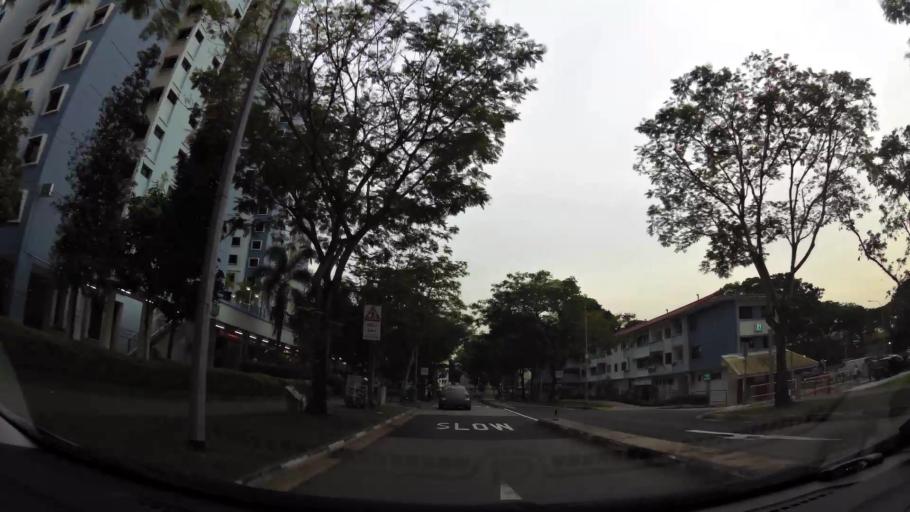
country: SG
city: Singapore
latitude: 1.3082
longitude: 103.8843
